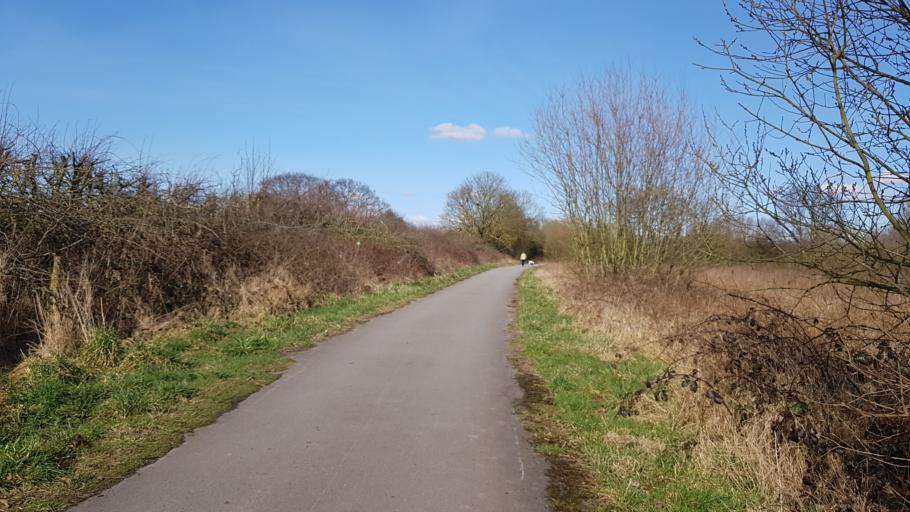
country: GB
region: England
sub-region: City of York
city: York
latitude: 53.9832
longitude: -1.0801
